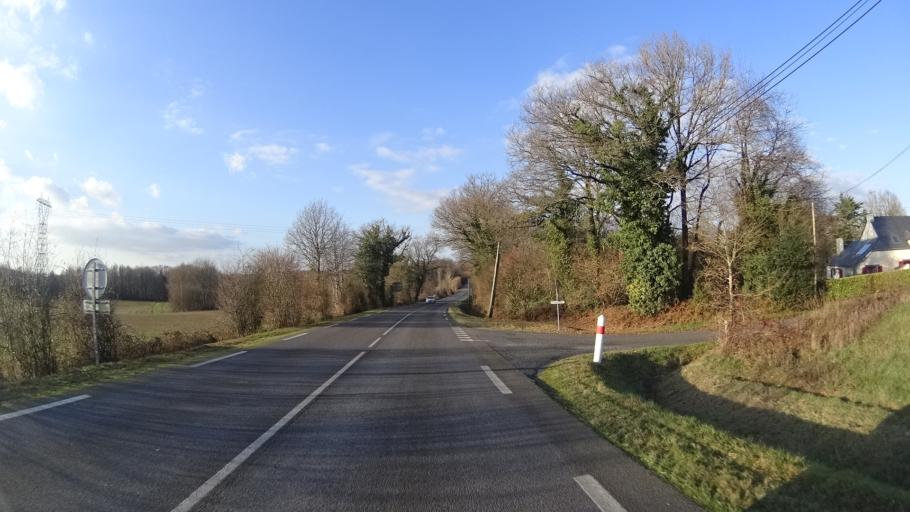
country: FR
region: Pays de la Loire
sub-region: Departement de la Loire-Atlantique
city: Fegreac
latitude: 47.5894
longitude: -2.0064
